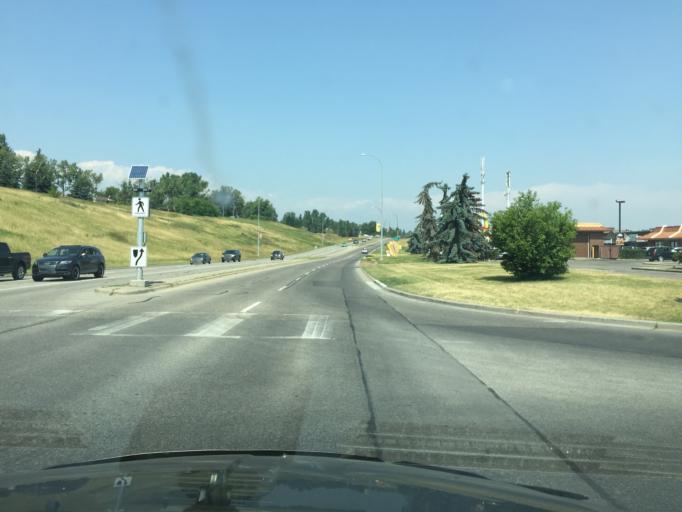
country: CA
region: Alberta
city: Calgary
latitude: 50.9272
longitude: -114.0300
